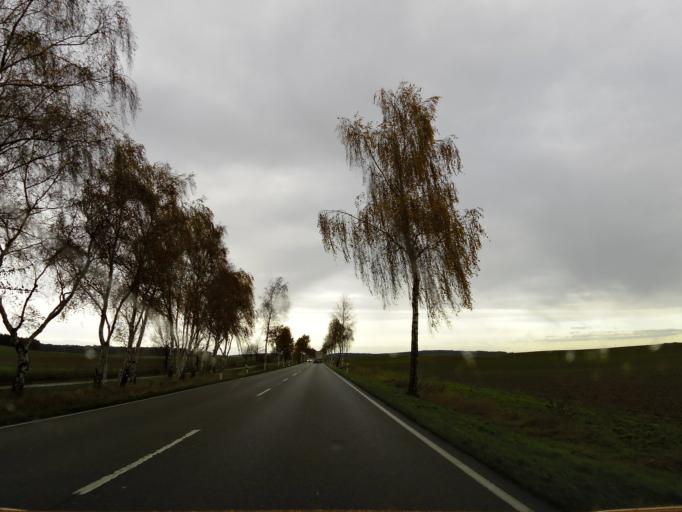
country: DE
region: Saxony-Anhalt
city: Gardelegen
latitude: 52.5816
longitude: 11.3531
